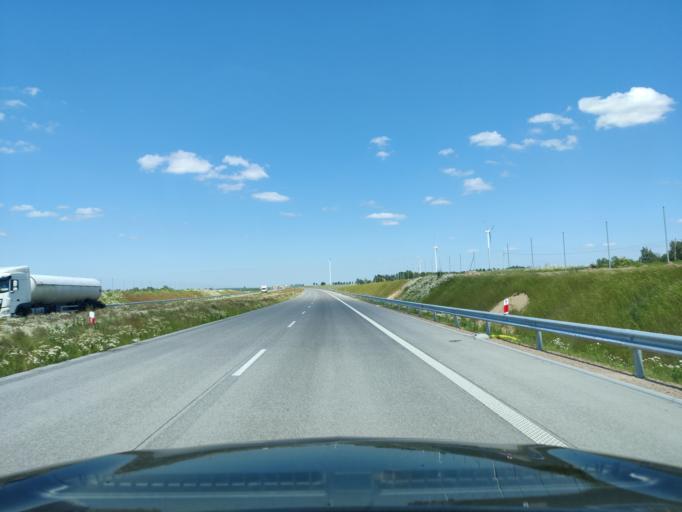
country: PL
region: Masovian Voivodeship
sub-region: Powiat mlawski
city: Wisniewo
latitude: 53.0378
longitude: 20.3556
